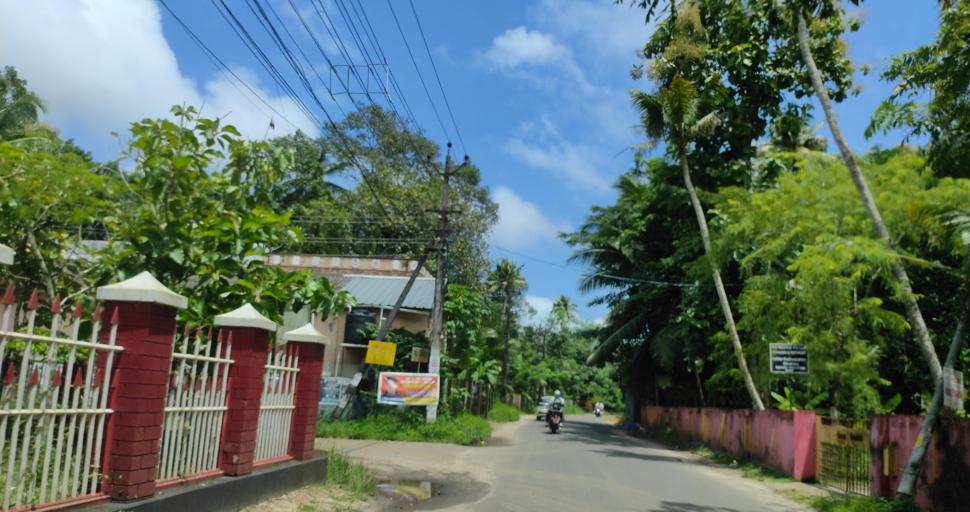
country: IN
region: Kerala
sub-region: Alappuzha
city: Vayalar
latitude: 9.7035
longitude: 76.3390
